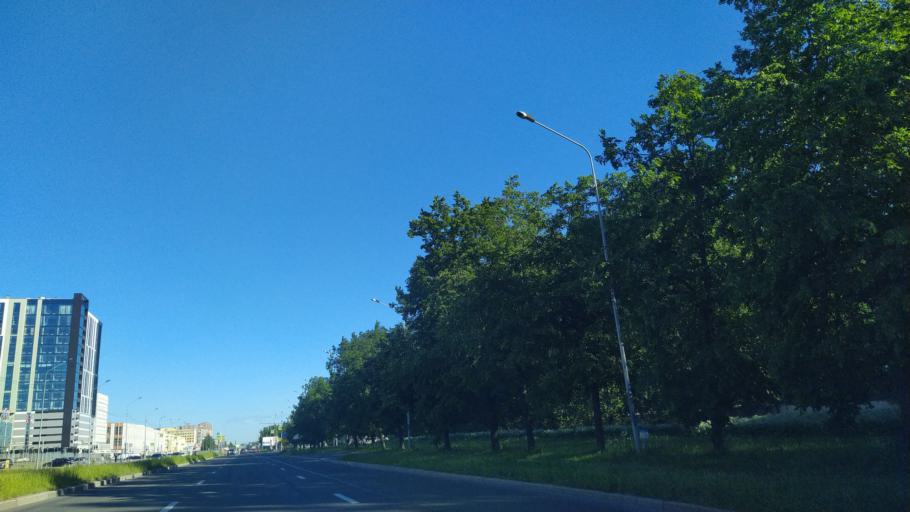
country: RU
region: St.-Petersburg
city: Kupchino
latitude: 59.8861
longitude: 30.3850
